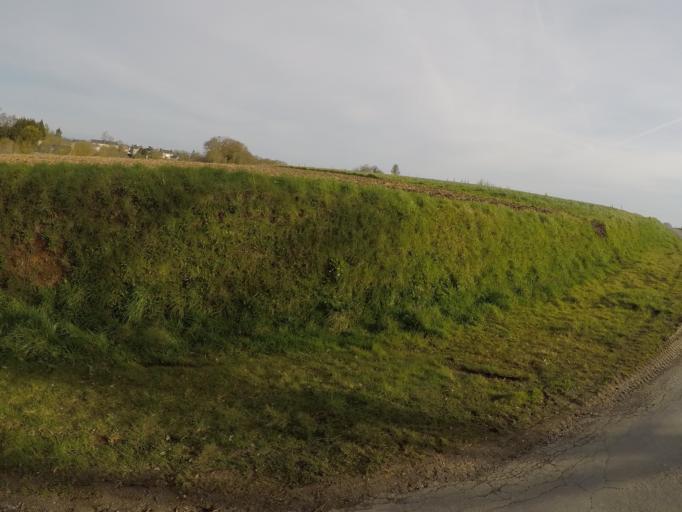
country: FR
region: Brittany
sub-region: Departement des Cotes-d'Armor
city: Plouagat
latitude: 48.5333
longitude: -2.9700
